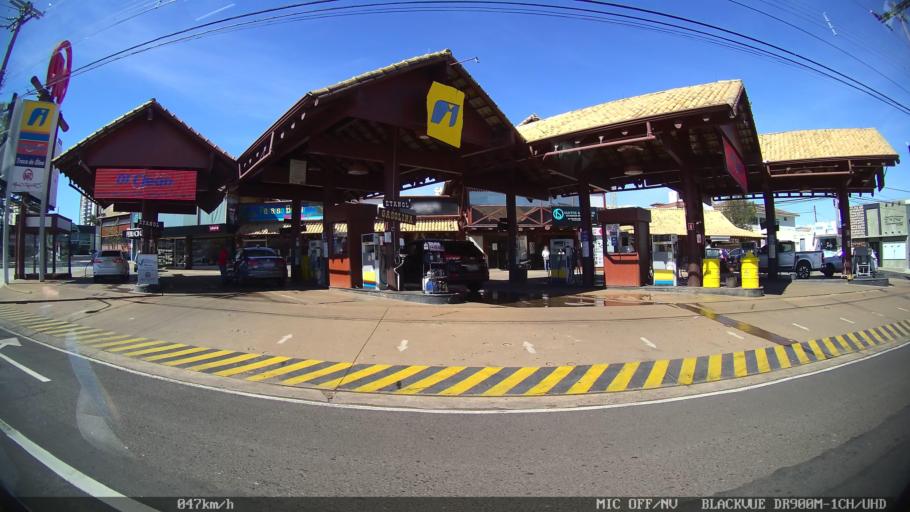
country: BR
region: Sao Paulo
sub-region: Franca
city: Franca
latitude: -20.5473
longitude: -47.4003
